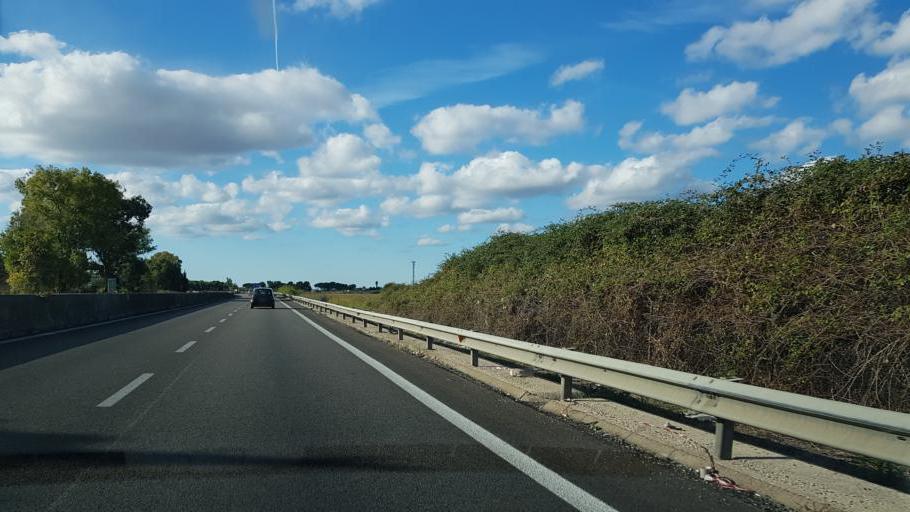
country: IT
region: Apulia
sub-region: Provincia di Lecce
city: Surbo
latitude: 40.3812
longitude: 18.1334
